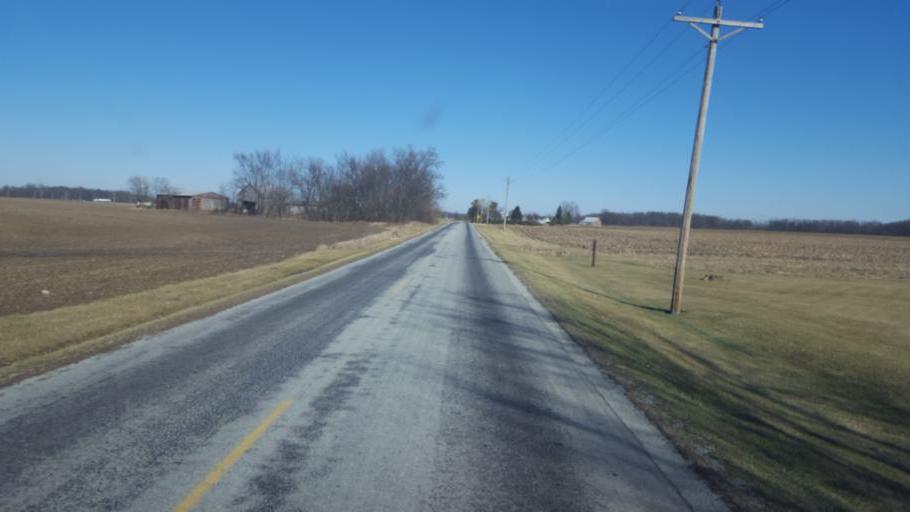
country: US
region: Ohio
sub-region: Hardin County
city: Kenton
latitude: 40.6362
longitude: -83.4804
